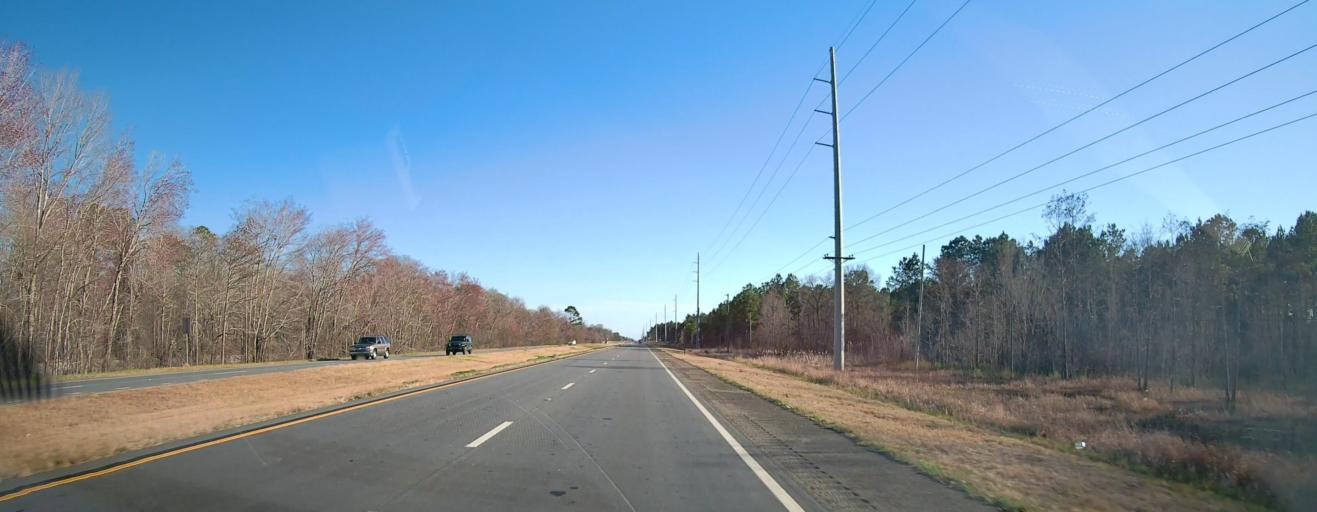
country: US
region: Georgia
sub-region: Lee County
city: Leesburg
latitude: 31.8813
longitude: -84.2431
